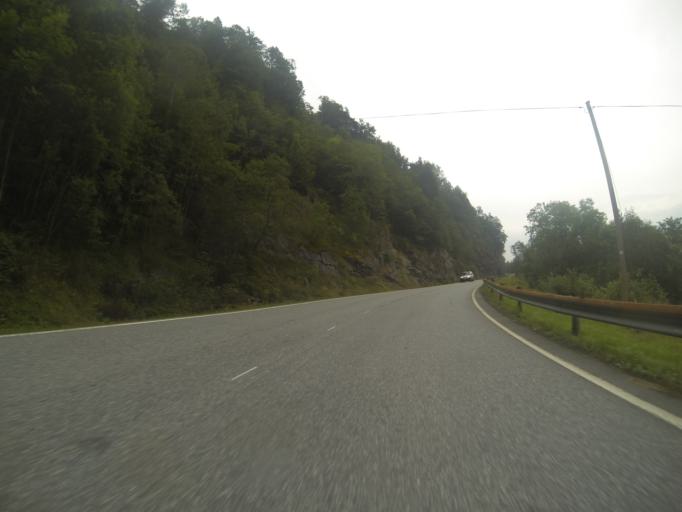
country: NO
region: Rogaland
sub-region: Suldal
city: Sand
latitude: 59.5388
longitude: 6.2535
